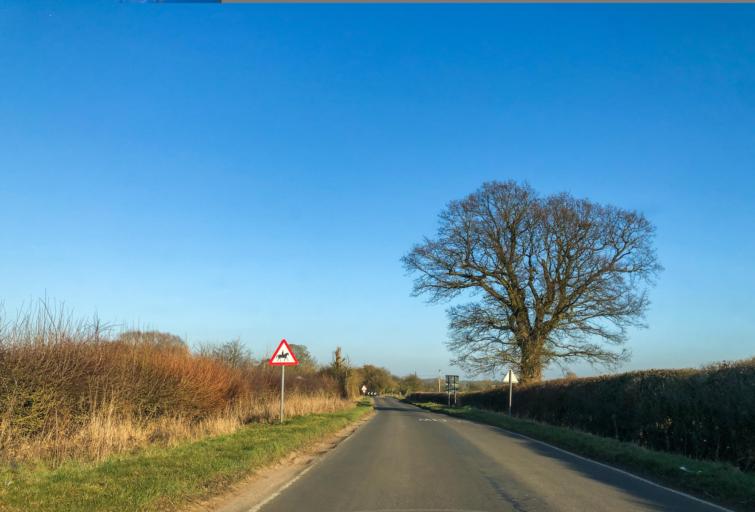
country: GB
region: England
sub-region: Warwickshire
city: Wellesbourne Mountford
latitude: 52.2059
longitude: -1.5474
